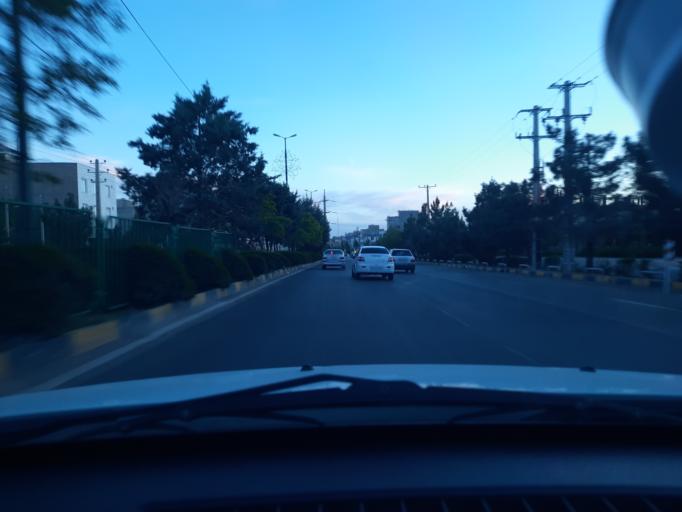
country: IR
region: Qazvin
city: Qazvin
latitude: 36.3074
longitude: 50.0122
